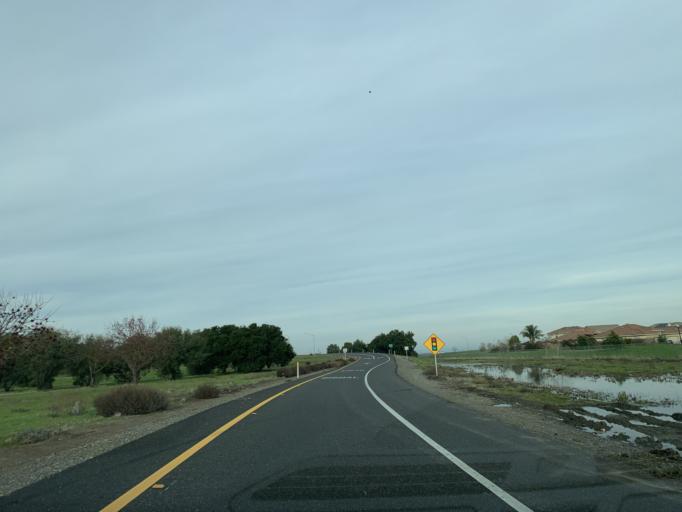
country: US
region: California
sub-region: Sacramento County
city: Elverta
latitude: 38.6832
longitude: -121.5395
